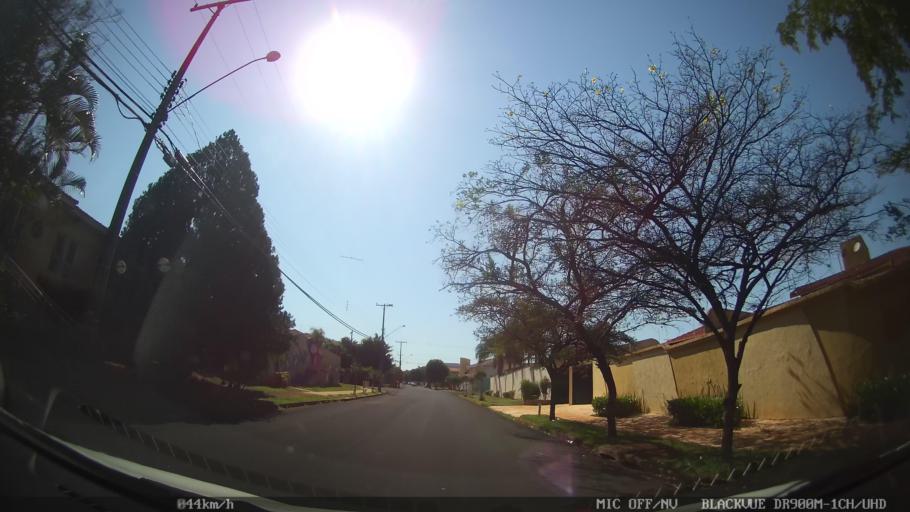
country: BR
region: Sao Paulo
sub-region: Ribeirao Preto
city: Ribeirao Preto
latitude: -21.2073
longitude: -47.7734
